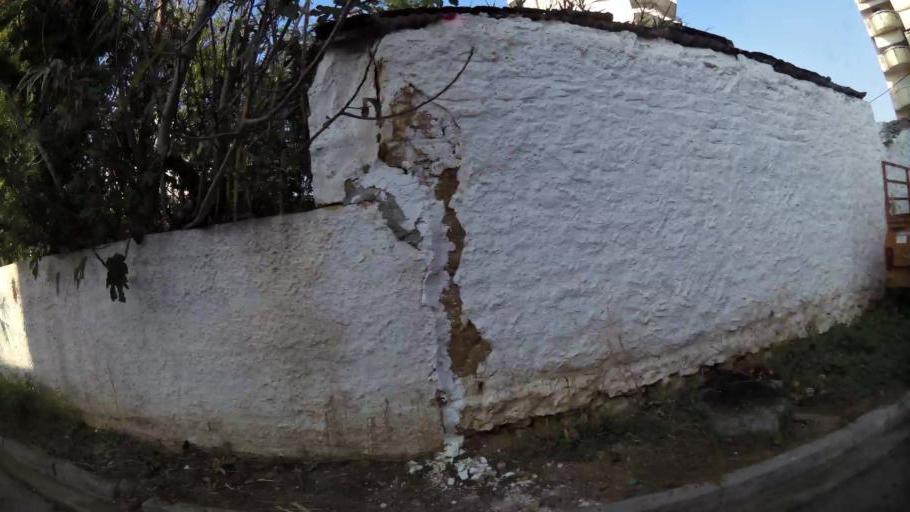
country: GR
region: Attica
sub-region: Nomarchia Anatolikis Attikis
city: Acharnes
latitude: 38.0862
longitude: 23.7408
